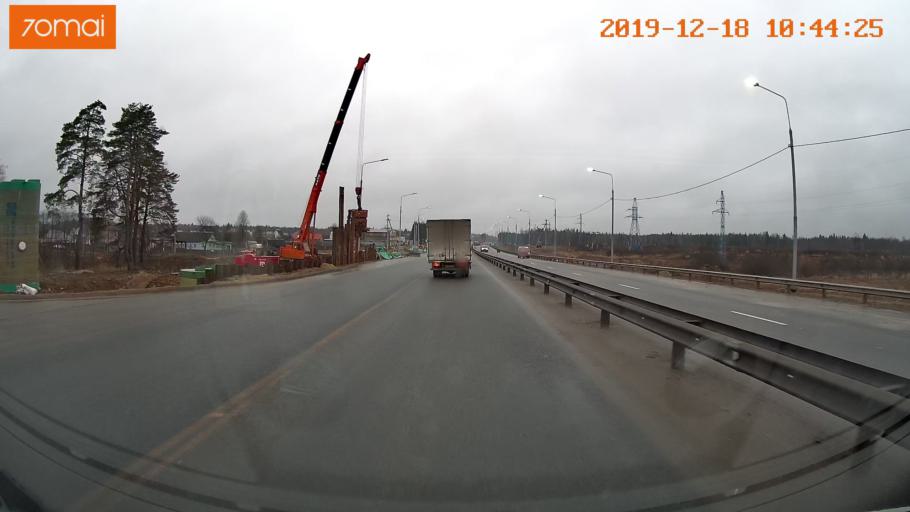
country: RU
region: Moskovskaya
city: Aprelevka
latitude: 55.4729
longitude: 37.0725
